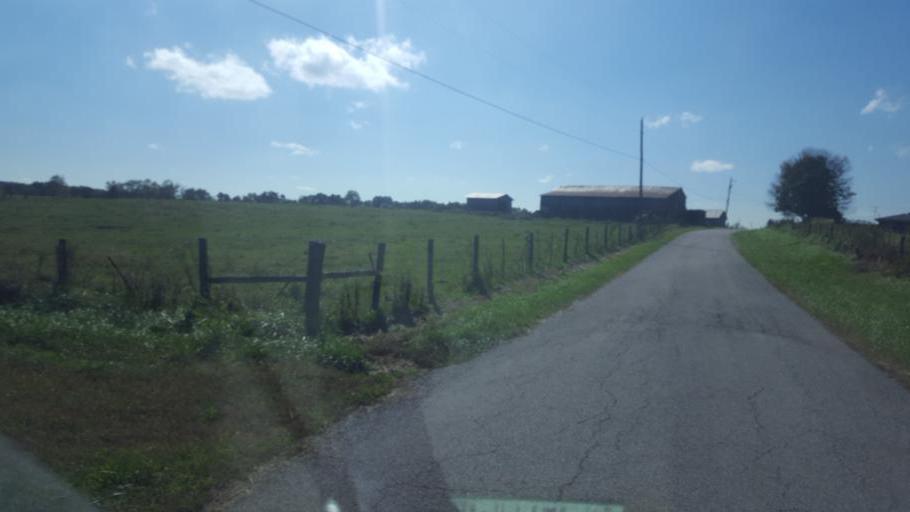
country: US
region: Kentucky
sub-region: Fleming County
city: Flemingsburg
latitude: 38.4590
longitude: -83.5297
